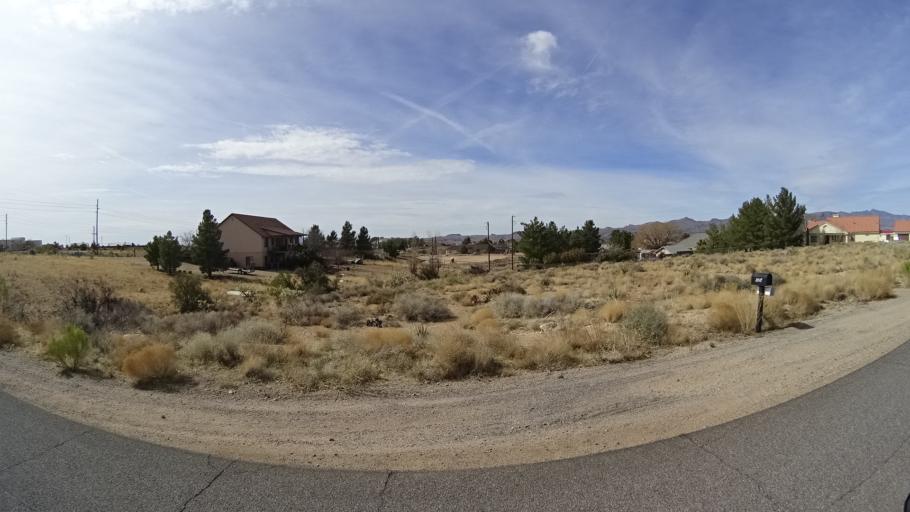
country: US
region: Arizona
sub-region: Mohave County
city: Kingman
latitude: 35.1816
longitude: -113.9845
